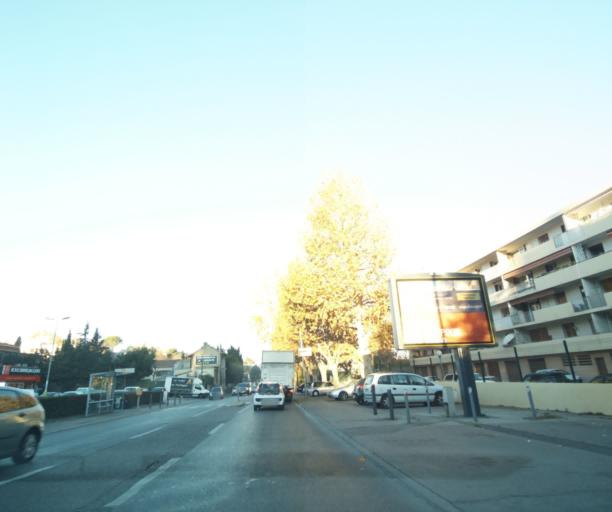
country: FR
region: Provence-Alpes-Cote d'Azur
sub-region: Departement des Bouches-du-Rhone
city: Marseille 12
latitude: 43.3262
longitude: 5.4396
